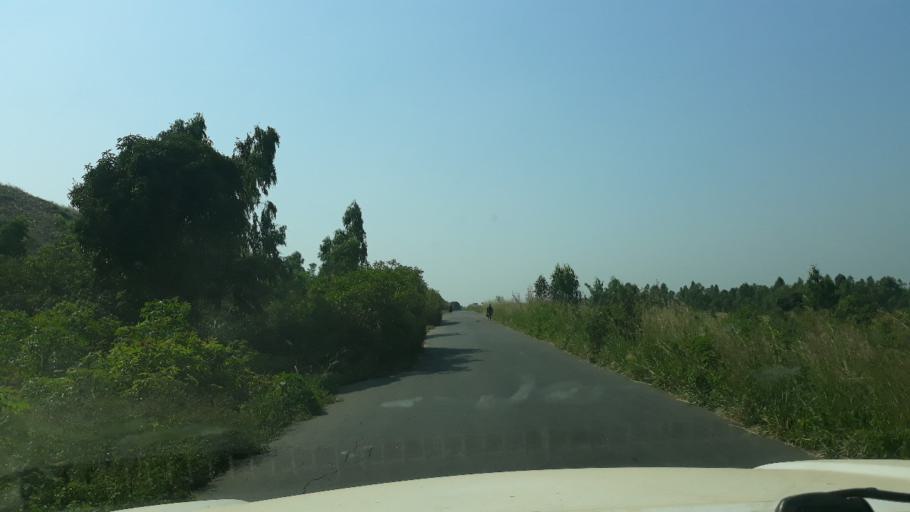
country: CD
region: South Kivu
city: Uvira
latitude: -3.2703
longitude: 29.1612
